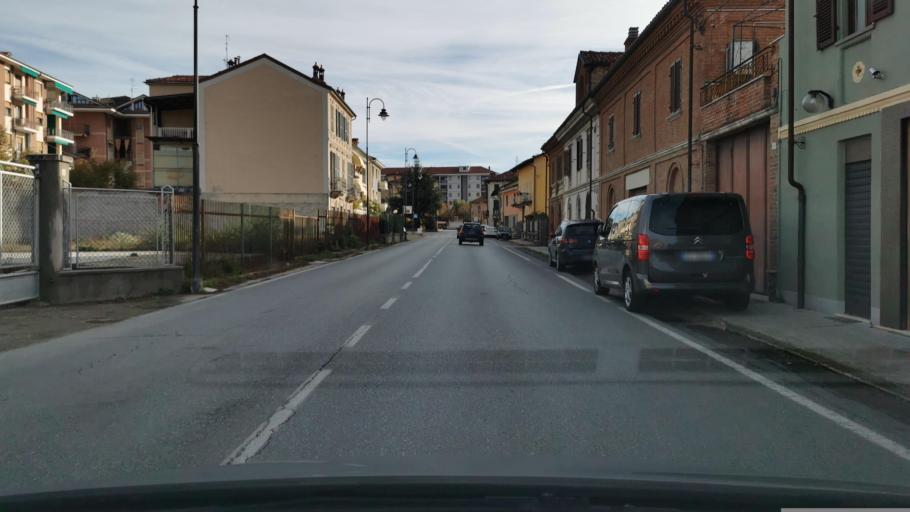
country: IT
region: Piedmont
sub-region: Provincia di Cuneo
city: Dogliani
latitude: 44.5325
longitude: 7.9431
